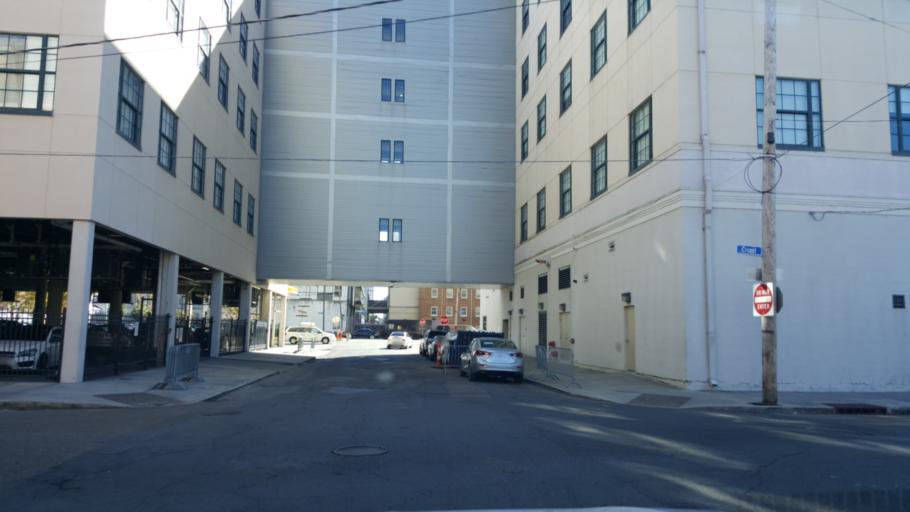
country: US
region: Louisiana
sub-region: Orleans Parish
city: New Orleans
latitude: 29.9576
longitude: -90.0734
